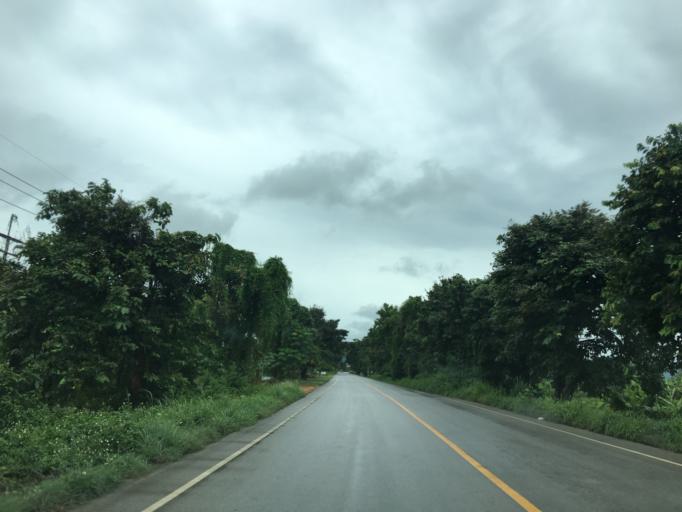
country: TH
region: Chiang Rai
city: Pa Daet
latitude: 19.4986
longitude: 99.9837
